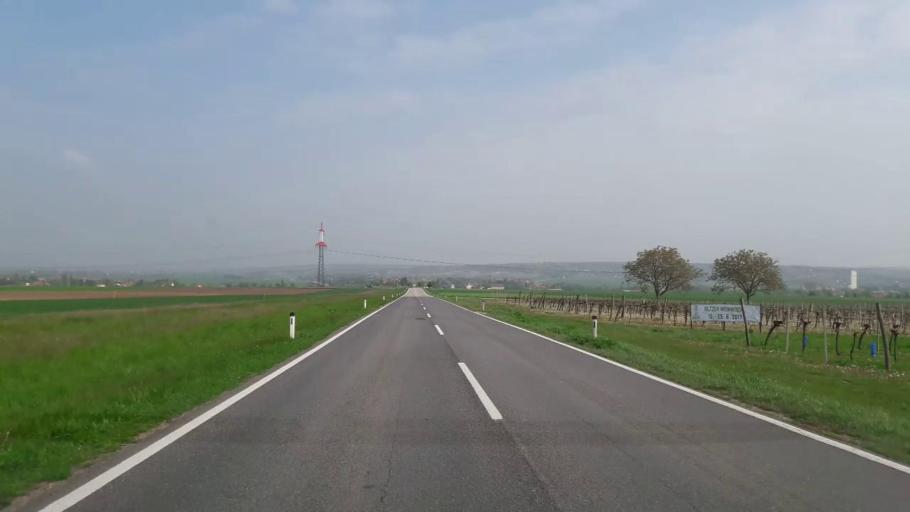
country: AT
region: Lower Austria
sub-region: Politischer Bezirk Hollabrunn
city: Haugsdorf
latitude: 48.6930
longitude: 16.0580
